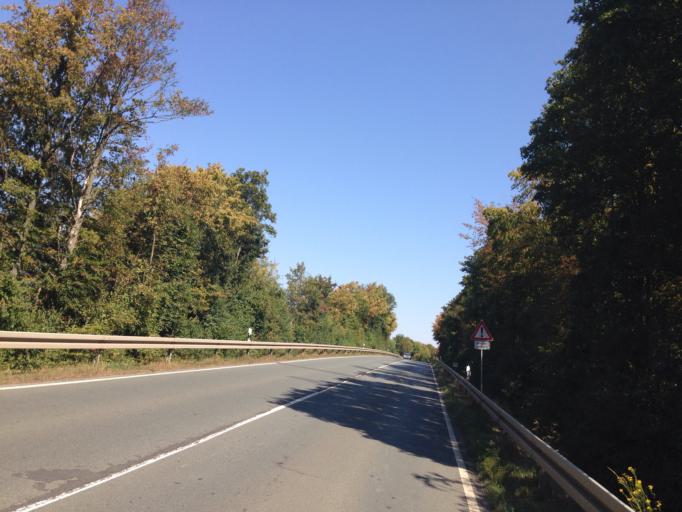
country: DE
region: Hesse
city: Allendorf an der Lahn
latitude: 50.5268
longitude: 8.5966
